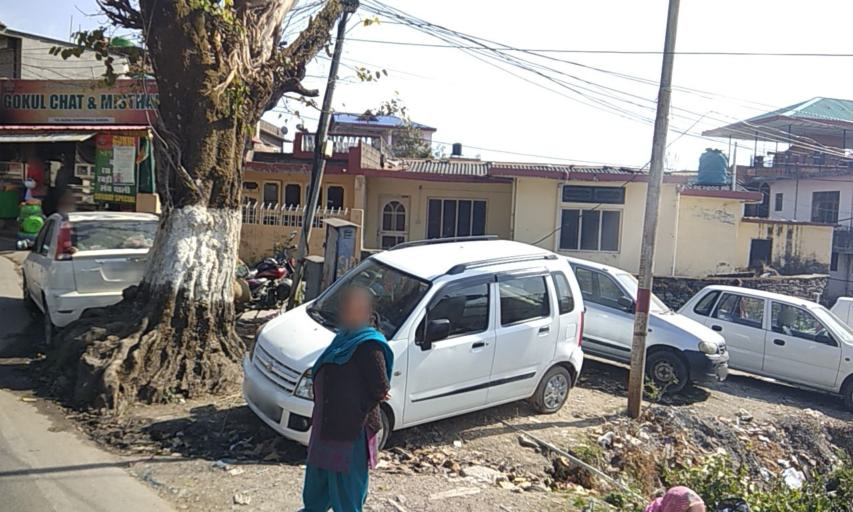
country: IN
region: Himachal Pradesh
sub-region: Kangra
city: Dharmsala
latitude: 32.1838
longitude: 76.3720
